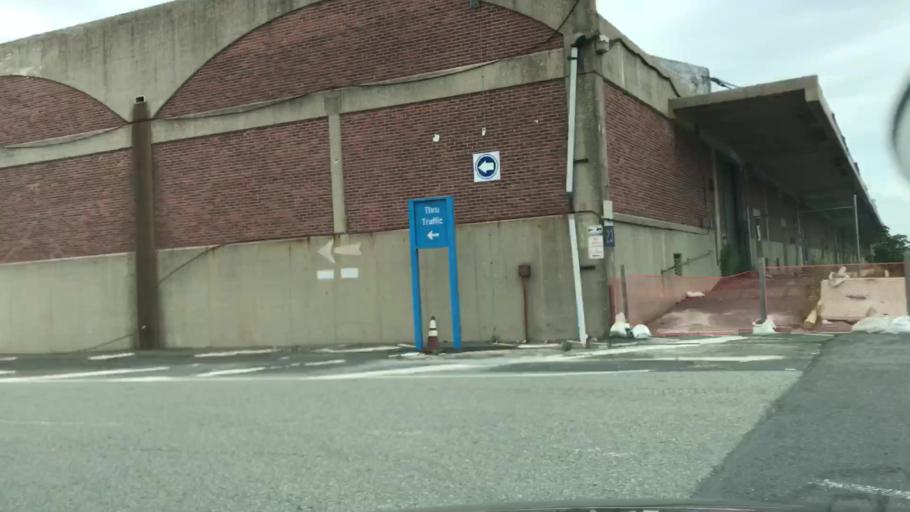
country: US
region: New Jersey
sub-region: Hudson County
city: Bayonne
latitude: 40.6659
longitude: -74.0771
